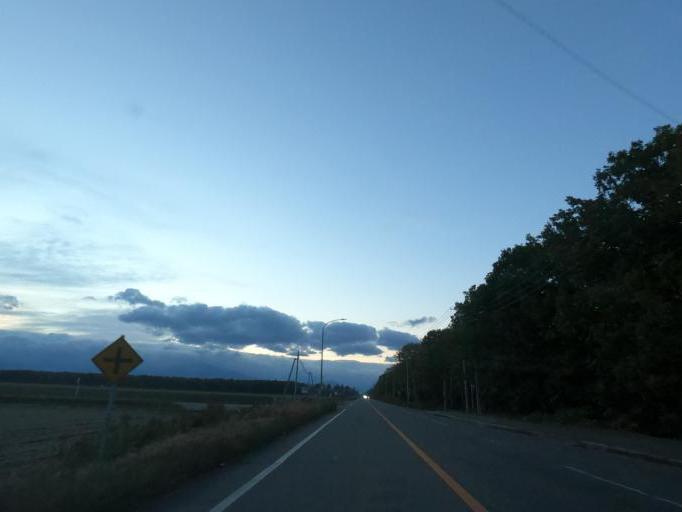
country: JP
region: Hokkaido
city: Obihiro
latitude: 42.6764
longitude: 143.1635
